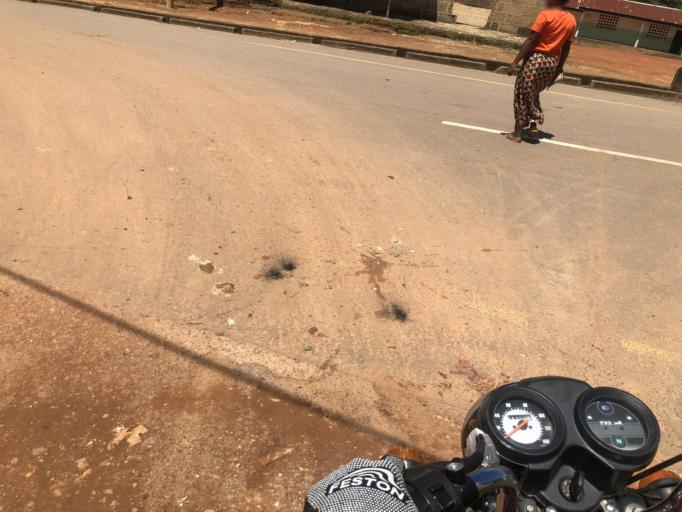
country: SL
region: Eastern Province
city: Koidu
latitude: 8.6419
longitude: -10.9664
